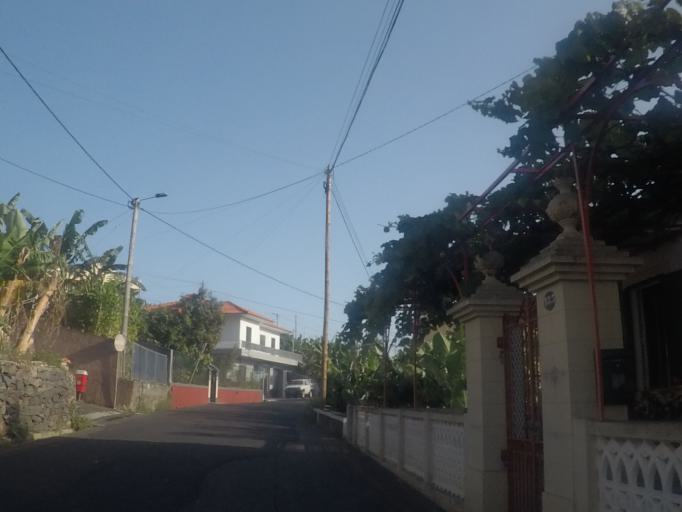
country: PT
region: Madeira
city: Ponta do Sol
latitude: 32.6847
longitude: -17.0949
